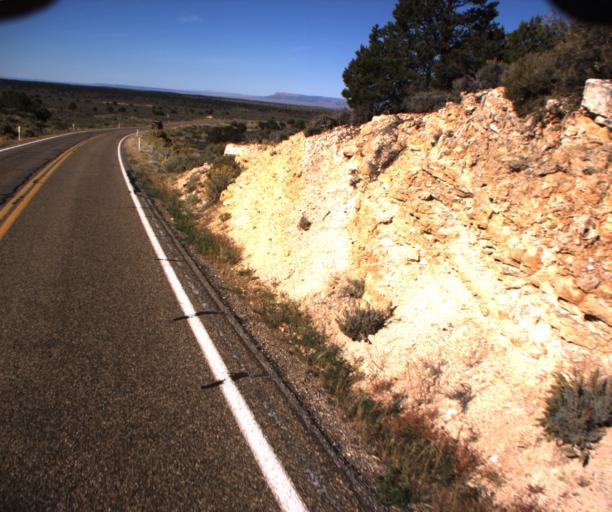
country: US
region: Arizona
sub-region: Coconino County
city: Fredonia
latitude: 36.8451
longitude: -112.2745
